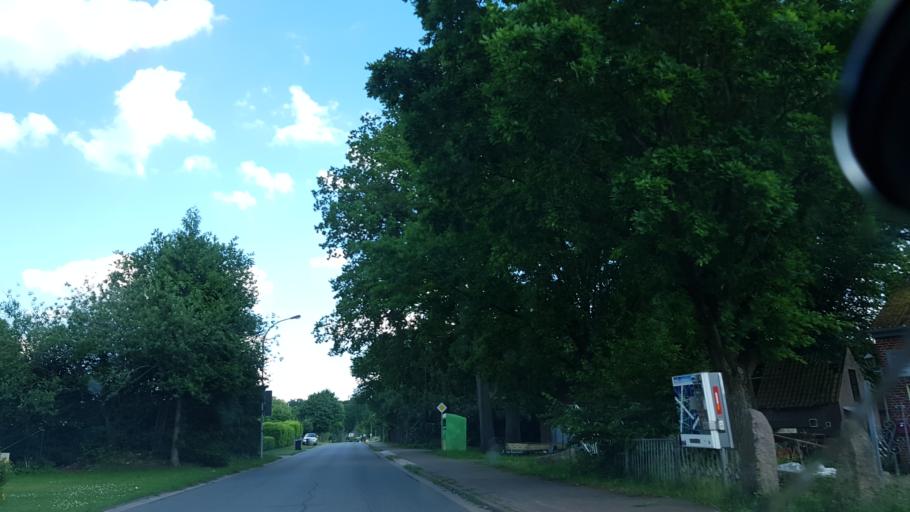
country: DE
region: Lower Saxony
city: Wenzendorf
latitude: 53.3512
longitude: 9.7696
